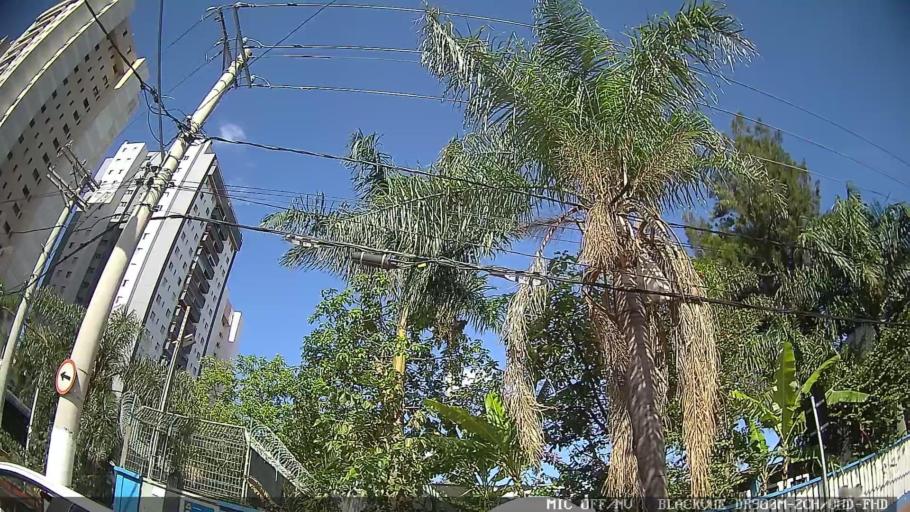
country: BR
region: Sao Paulo
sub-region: Sao Paulo
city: Sao Paulo
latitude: -23.5800
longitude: -46.6060
